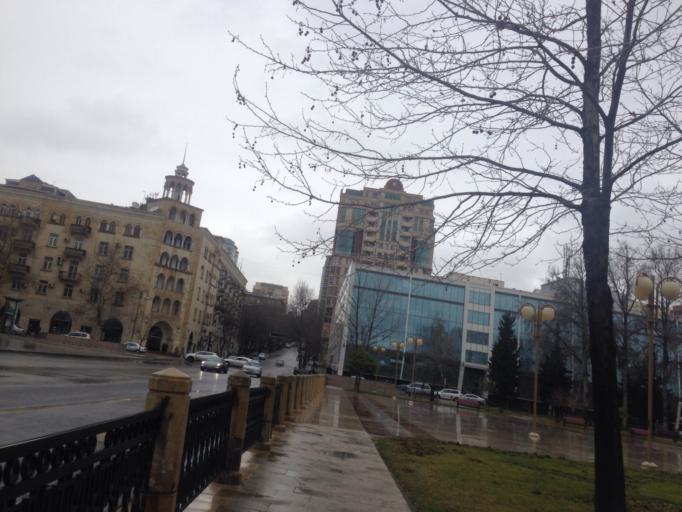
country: AZ
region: Baki
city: Baku
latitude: 40.3776
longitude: 49.8426
